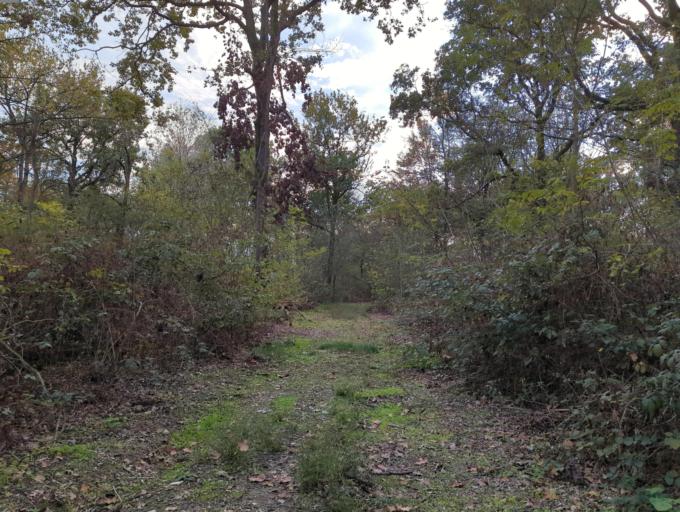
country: IT
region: Piedmont
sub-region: Provincia di Vercelli
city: Palazzolo Vercellese
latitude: 45.2125
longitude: 8.2596
